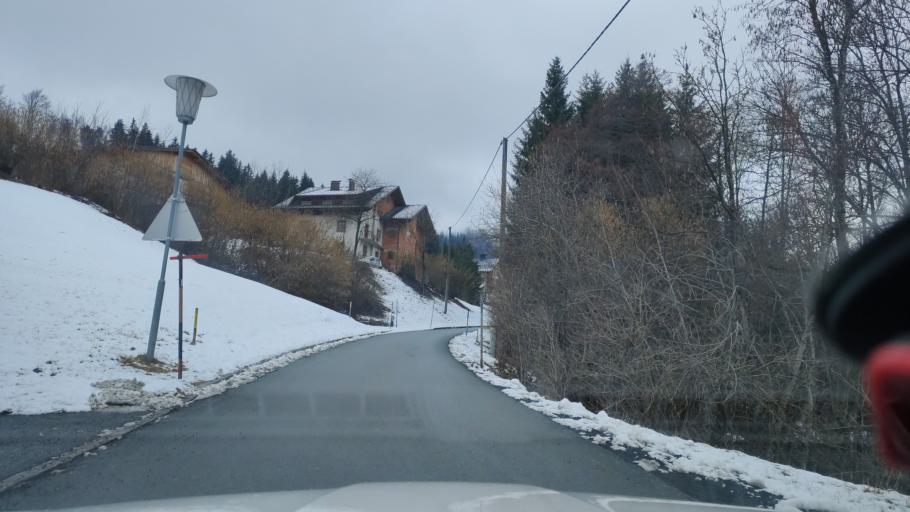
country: AT
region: Carinthia
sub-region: Politischer Bezirk Hermagor
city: Hermagor
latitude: 46.6277
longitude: 13.3603
